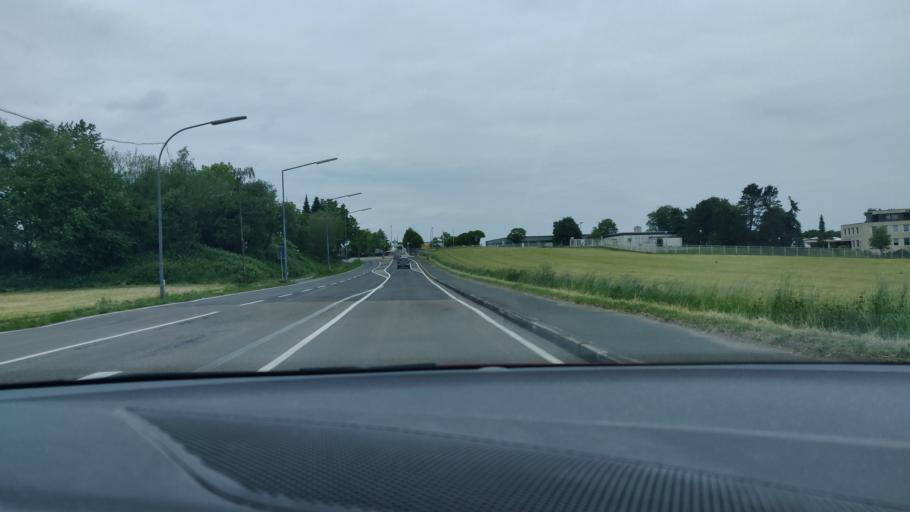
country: DE
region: North Rhine-Westphalia
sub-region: Regierungsbezirk Dusseldorf
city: Velbert
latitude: 51.3078
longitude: 7.0663
